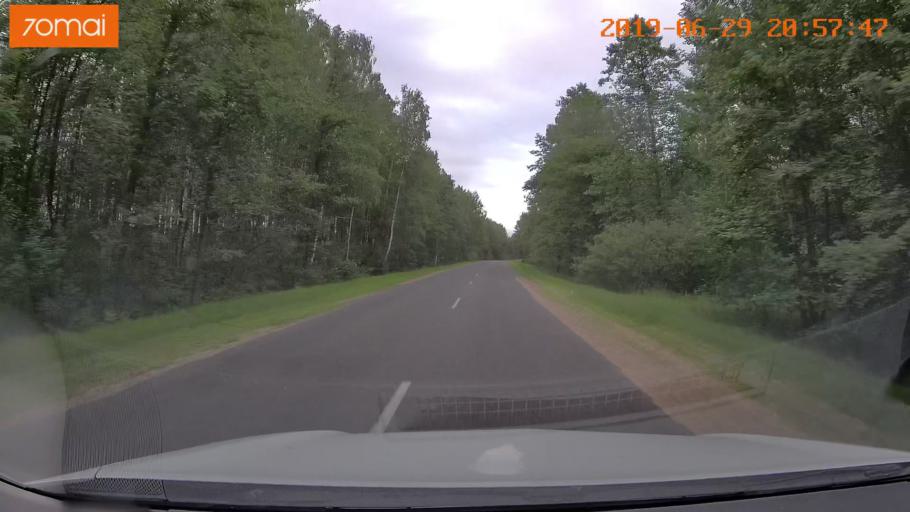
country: BY
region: Brest
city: Hantsavichy
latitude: 52.7235
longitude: 26.3747
